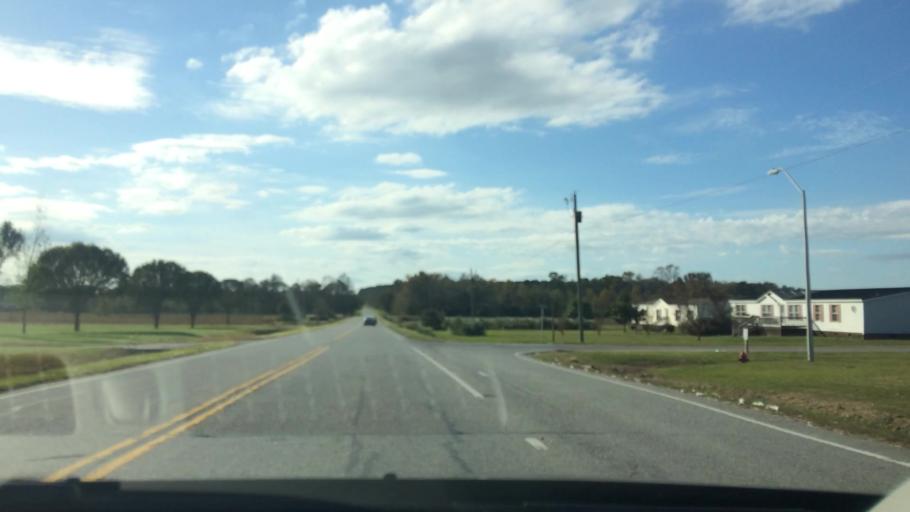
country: US
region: North Carolina
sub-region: Greene County
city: Snow Hill
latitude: 35.4420
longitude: -77.8111
